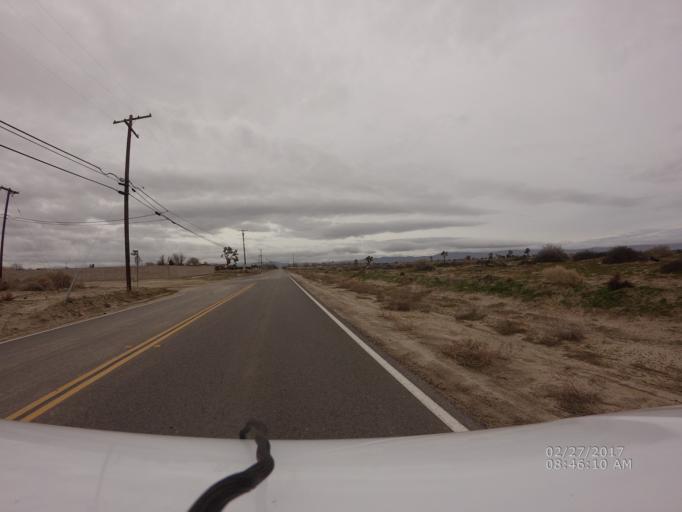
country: US
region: California
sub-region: Los Angeles County
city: Lancaster
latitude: 34.7175
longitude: -118.0772
